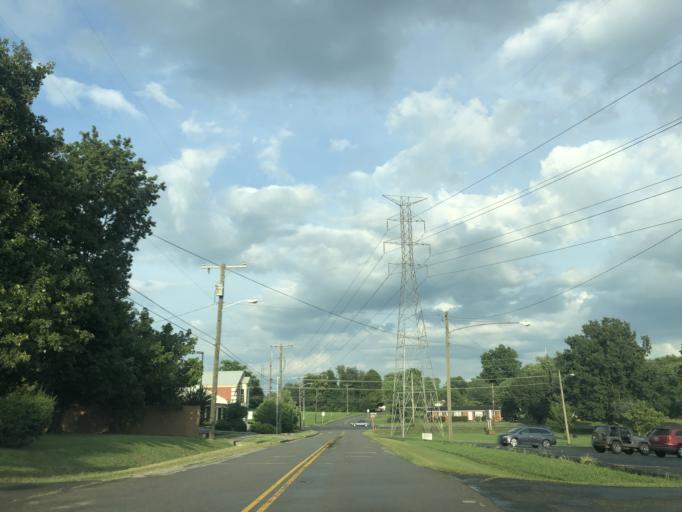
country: US
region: Tennessee
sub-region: Davidson County
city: Lakewood
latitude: 36.1567
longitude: -86.6667
